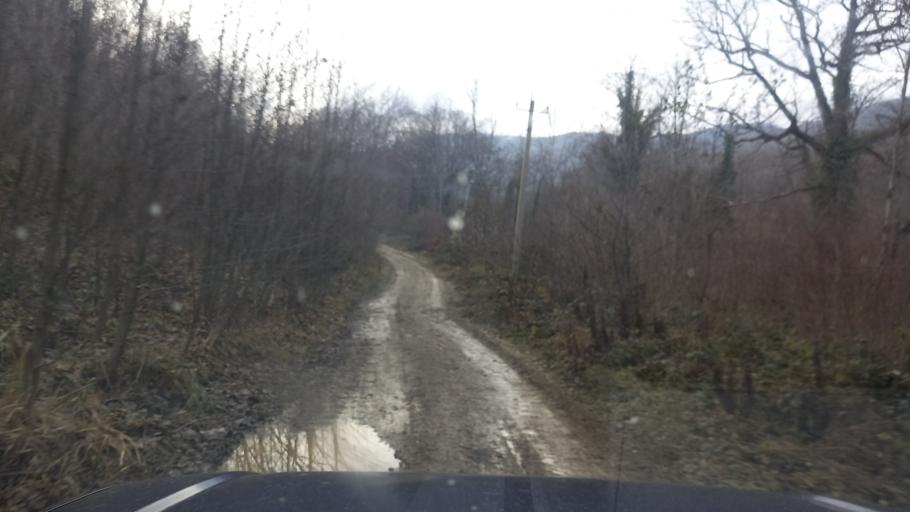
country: RU
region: Krasnodarskiy
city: Neftegorsk
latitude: 44.2184
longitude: 39.7238
